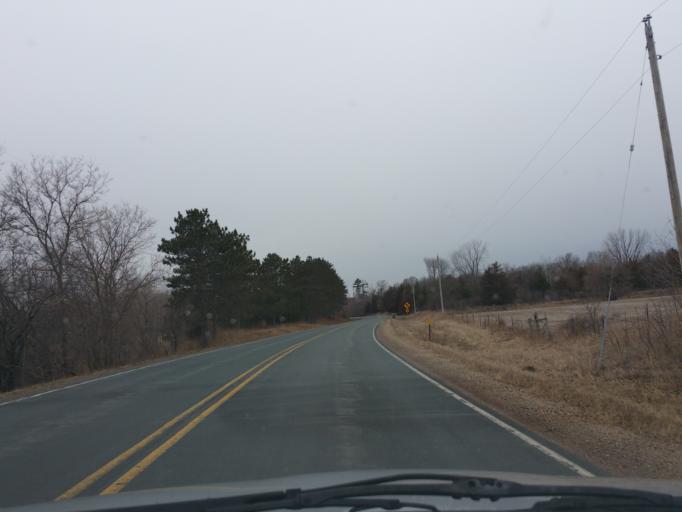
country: US
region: Wisconsin
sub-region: Saint Croix County
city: Roberts
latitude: 45.0358
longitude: -92.6327
